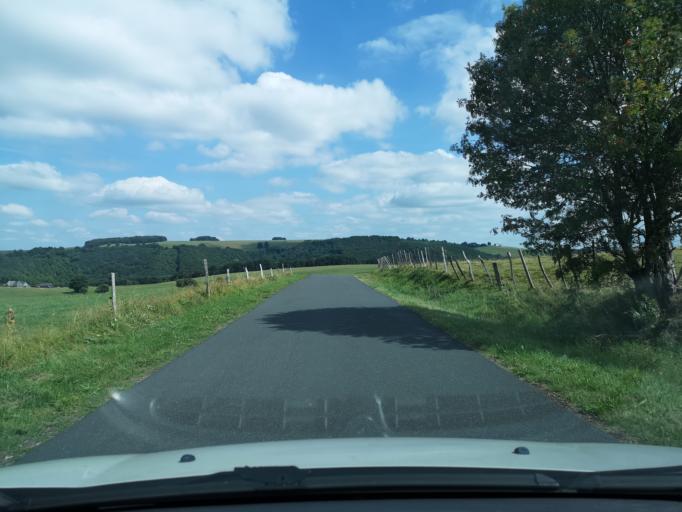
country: FR
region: Auvergne
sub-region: Departement du Puy-de-Dome
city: Mont-Dore
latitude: 45.5000
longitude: 2.9304
